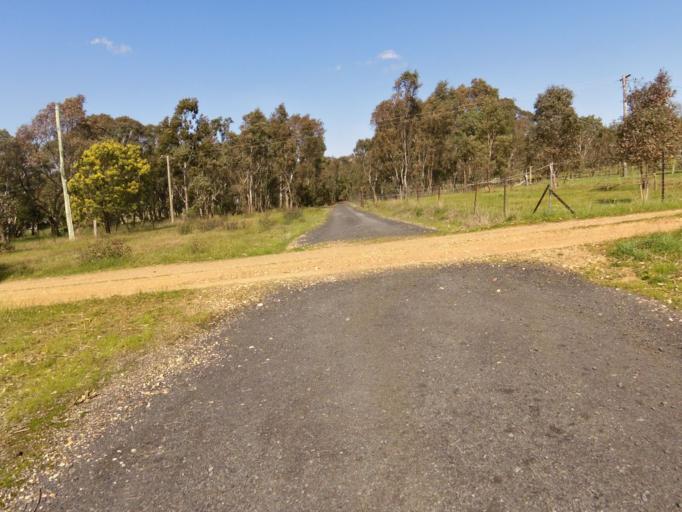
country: AU
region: Victoria
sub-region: Murrindindi
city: Alexandra
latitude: -36.9939
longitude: 145.7398
